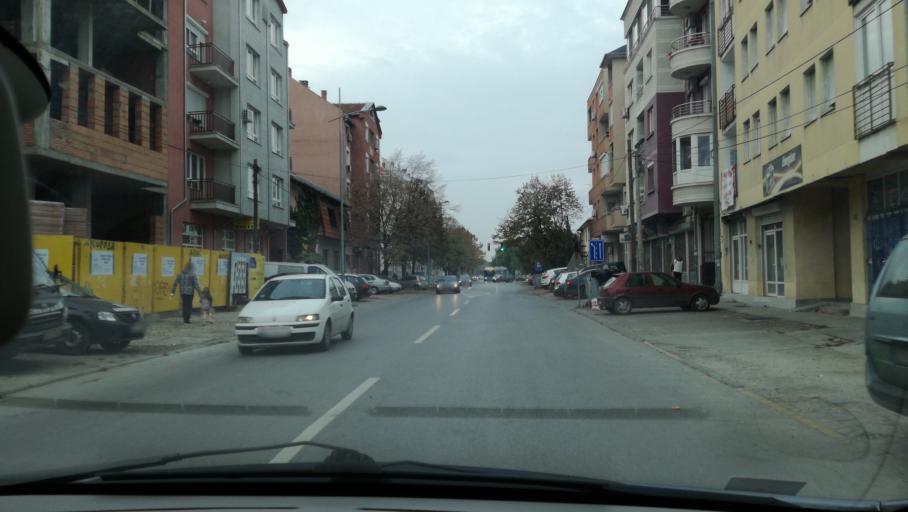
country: RS
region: Autonomna Pokrajina Vojvodina
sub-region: Juznobacki Okrug
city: Novi Sad
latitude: 45.2639
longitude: 19.8381
